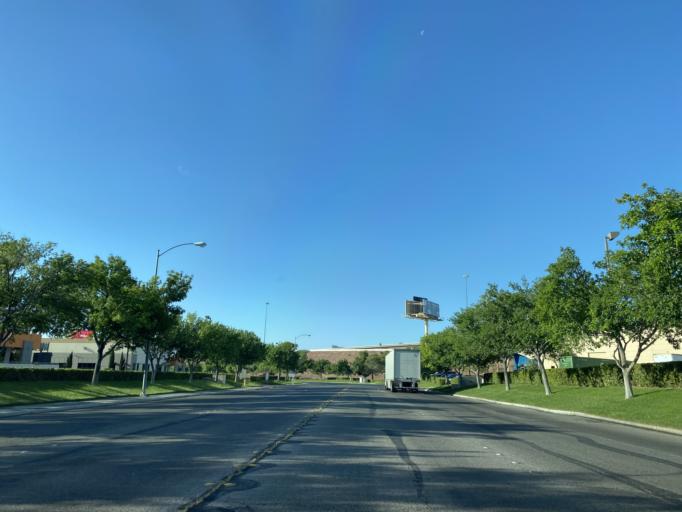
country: US
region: Nevada
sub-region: Clark County
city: Paradise
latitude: 36.0647
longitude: -115.1463
